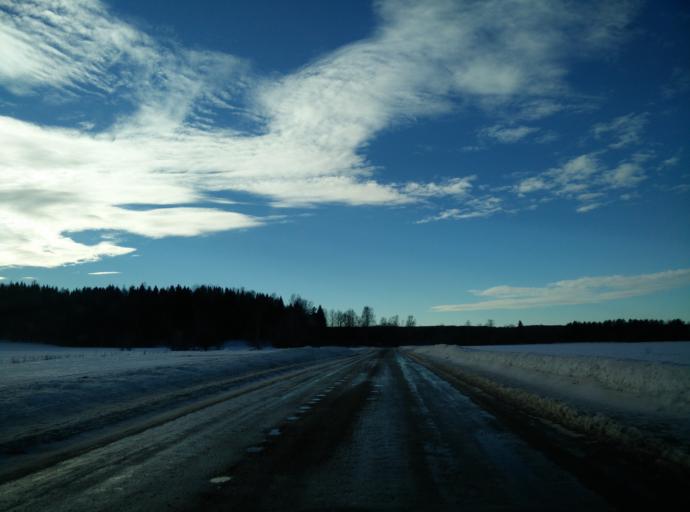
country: SE
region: Vaesternorrland
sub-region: Sundsvalls Kommun
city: Skottsund
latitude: 62.2787
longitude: 17.4001
